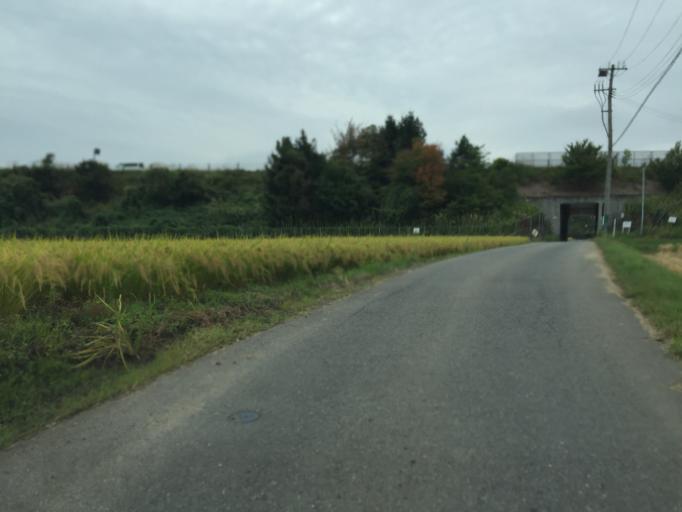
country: JP
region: Fukushima
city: Kitakata
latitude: 37.5286
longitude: 139.9384
